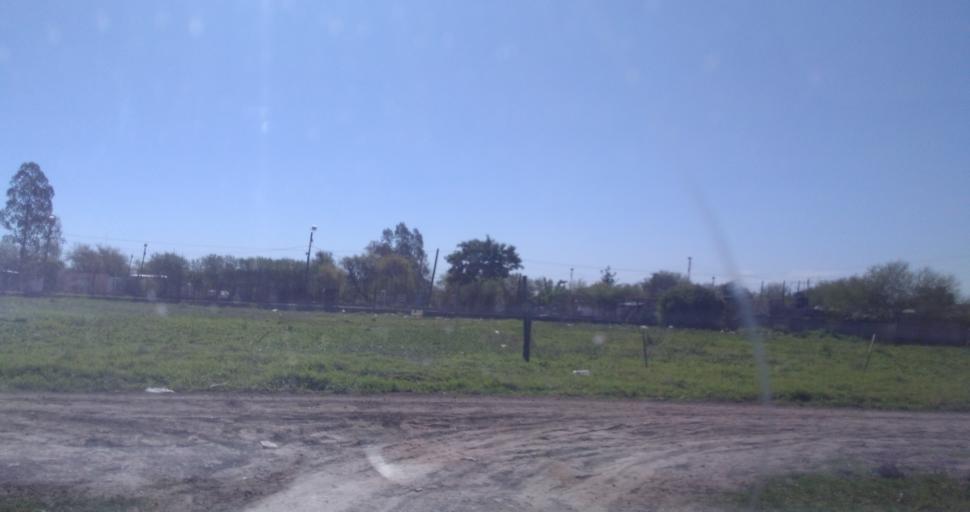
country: AR
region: Chaco
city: Resistencia
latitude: -27.4812
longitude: -59.0021
